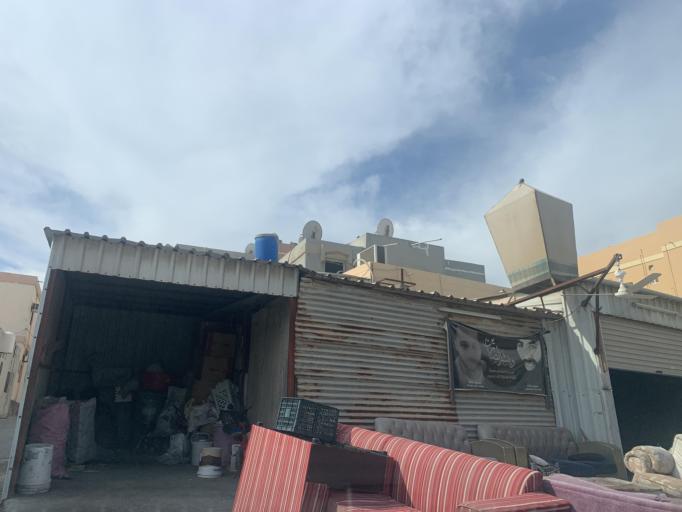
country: BH
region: Central Governorate
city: Madinat Hamad
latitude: 26.1190
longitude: 50.4817
